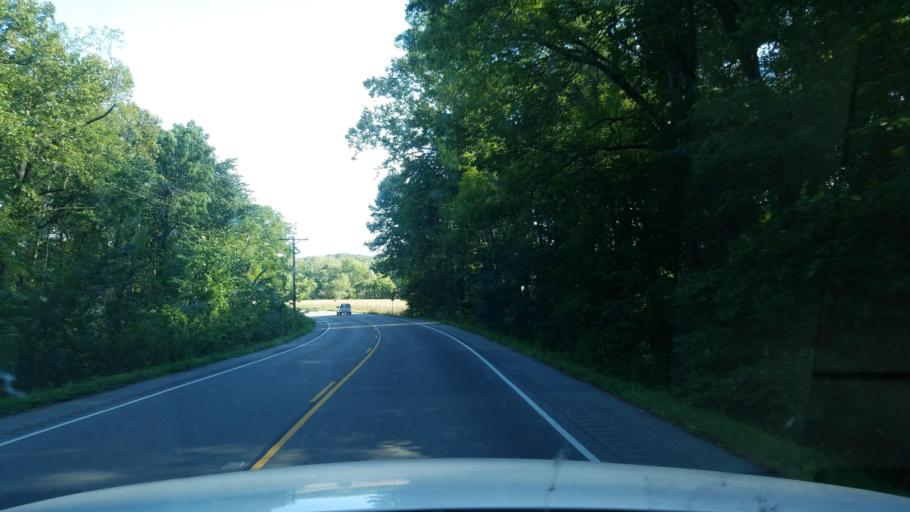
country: US
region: Illinois
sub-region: Saline County
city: Harrisburg
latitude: 37.5973
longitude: -88.4574
